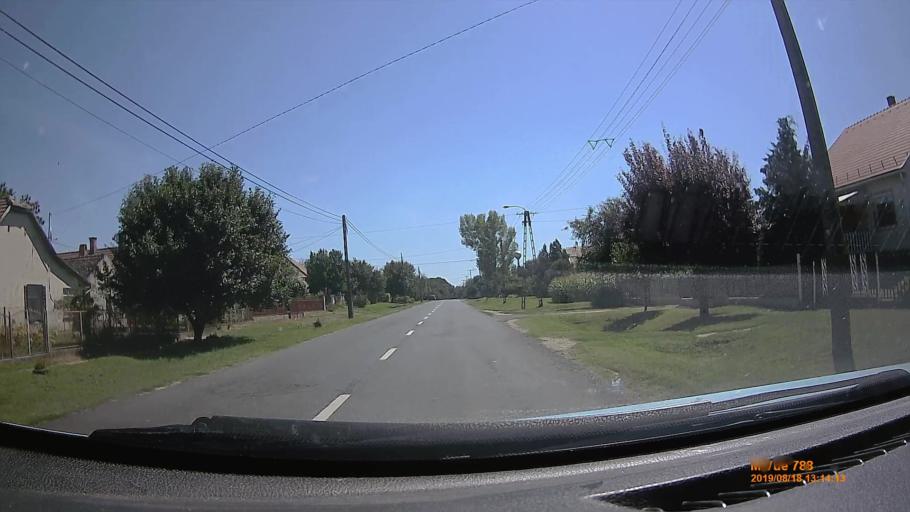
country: HU
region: Fejer
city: Sarbogard
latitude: 46.8767
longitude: 18.5387
